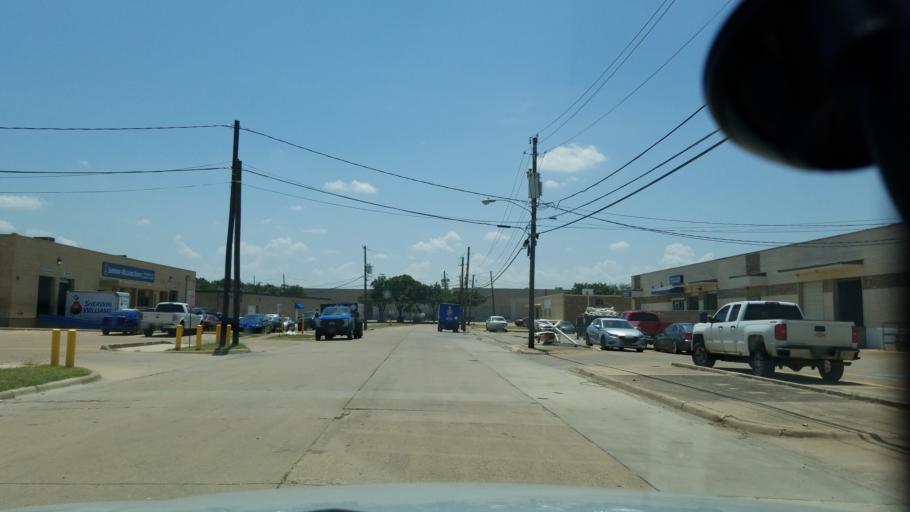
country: US
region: Texas
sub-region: Dallas County
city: Farmers Branch
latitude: 32.8922
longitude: -96.8861
